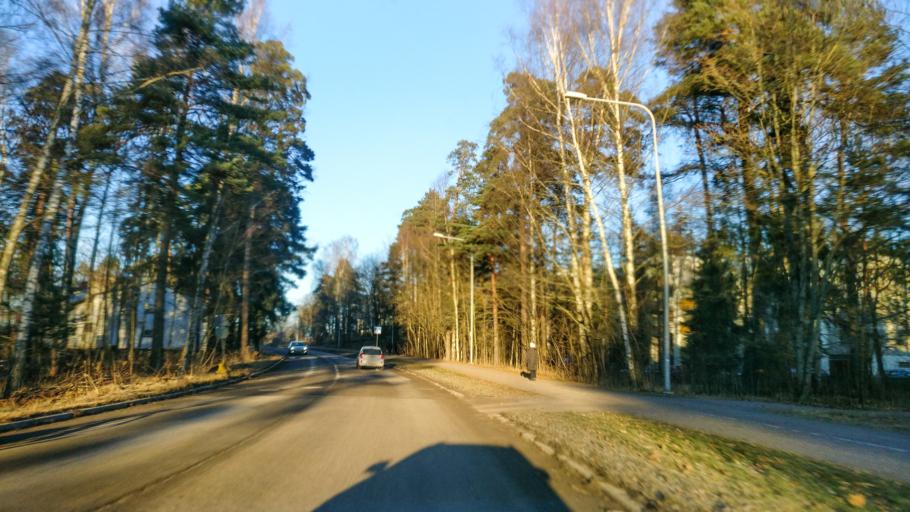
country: FI
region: Uusimaa
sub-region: Helsinki
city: Vantaa
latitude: 60.1813
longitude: 25.0509
